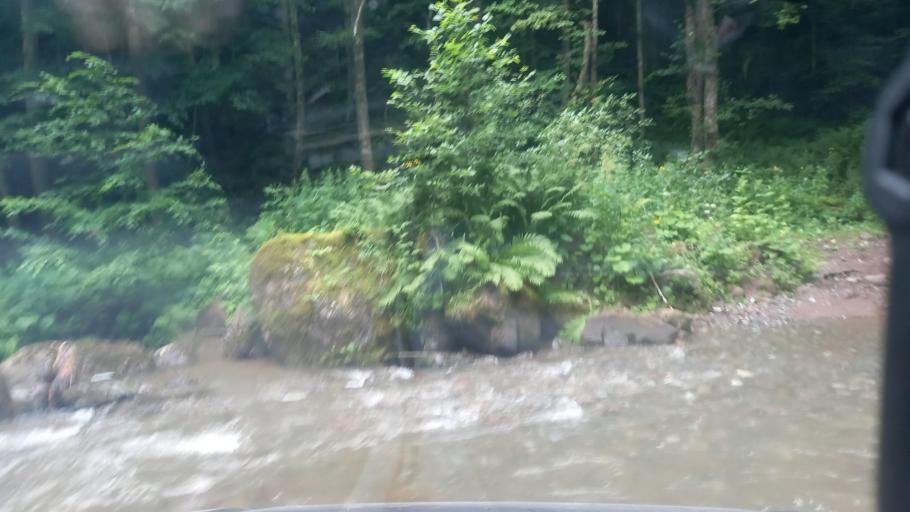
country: RU
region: Karachayevo-Cherkesiya
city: Kurdzhinovo
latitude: 43.8133
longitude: 40.8823
